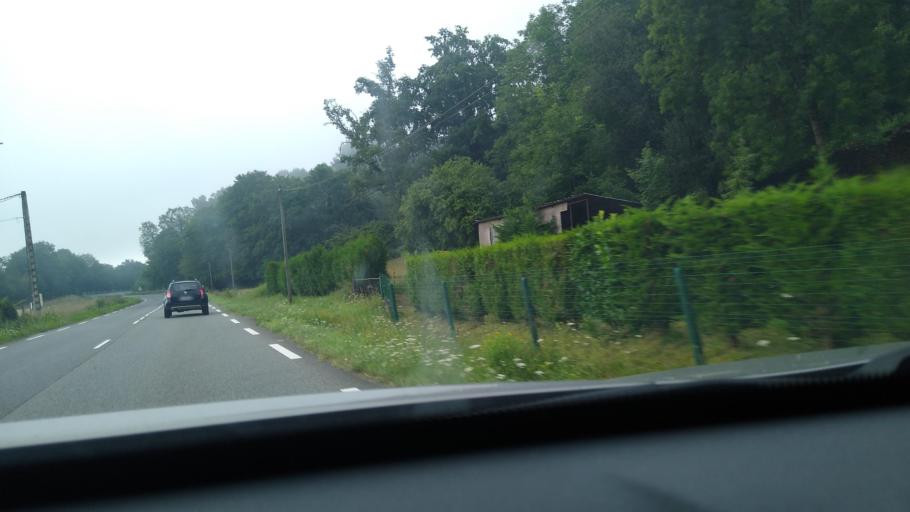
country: FR
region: Midi-Pyrenees
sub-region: Departement de la Haute-Garonne
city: Salies-du-Salat
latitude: 43.0742
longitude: 0.9627
